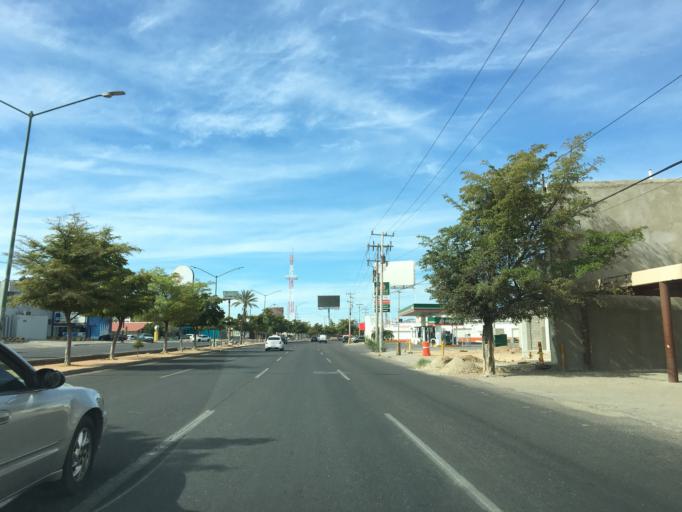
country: MX
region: Sonora
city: Hermosillo
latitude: 29.0467
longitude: -110.9625
